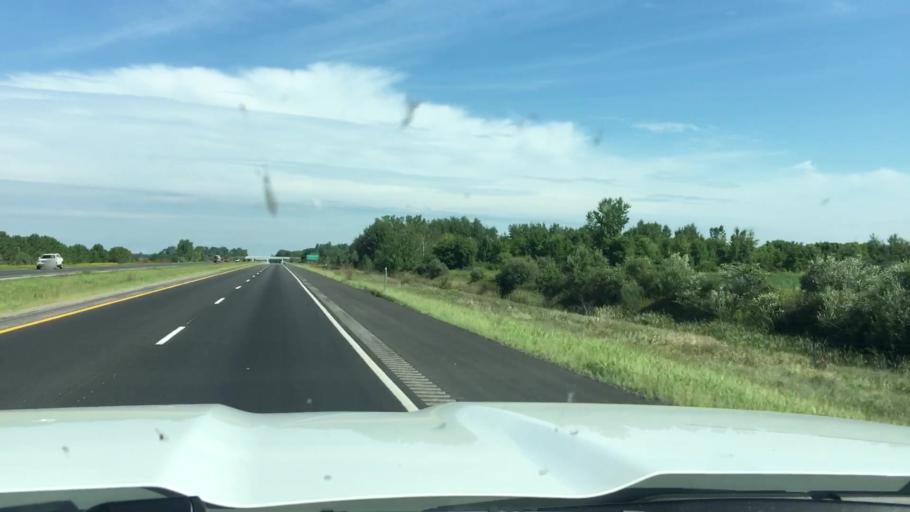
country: US
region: Michigan
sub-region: Saginaw County
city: Freeland
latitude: 43.5576
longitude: -84.1376
